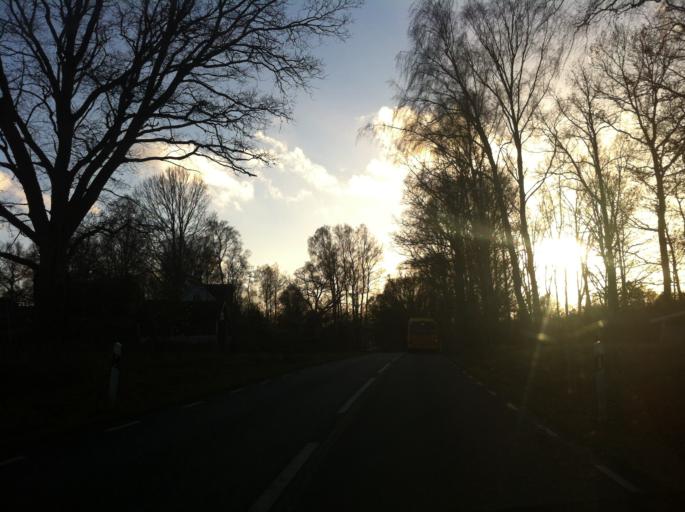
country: SE
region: Skane
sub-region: Hassleholms Kommun
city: Hastveda
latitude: 56.1864
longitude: 13.9492
